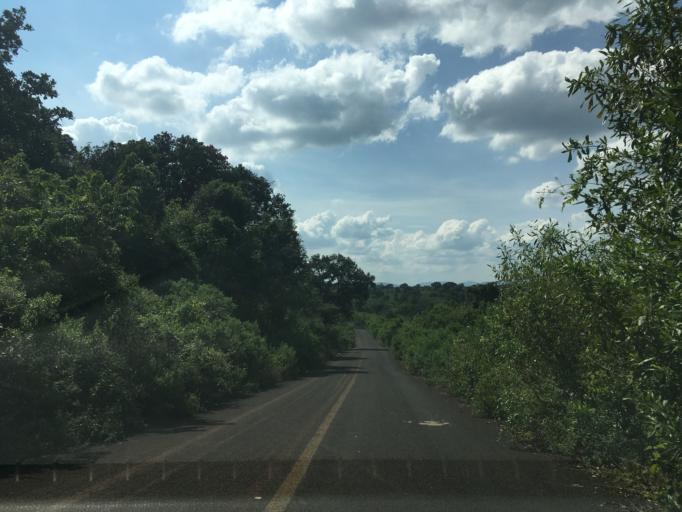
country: MX
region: Mexico
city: El Guayabito
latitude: 19.8799
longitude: -102.4973
